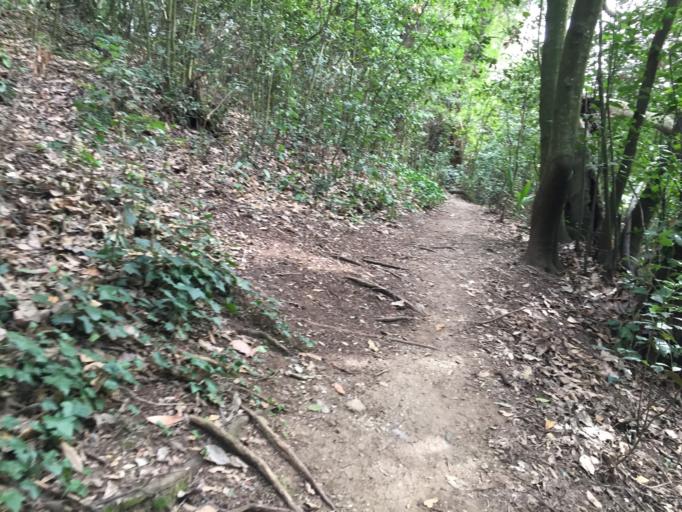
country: VA
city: Vatican City
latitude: 41.8845
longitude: 12.4454
